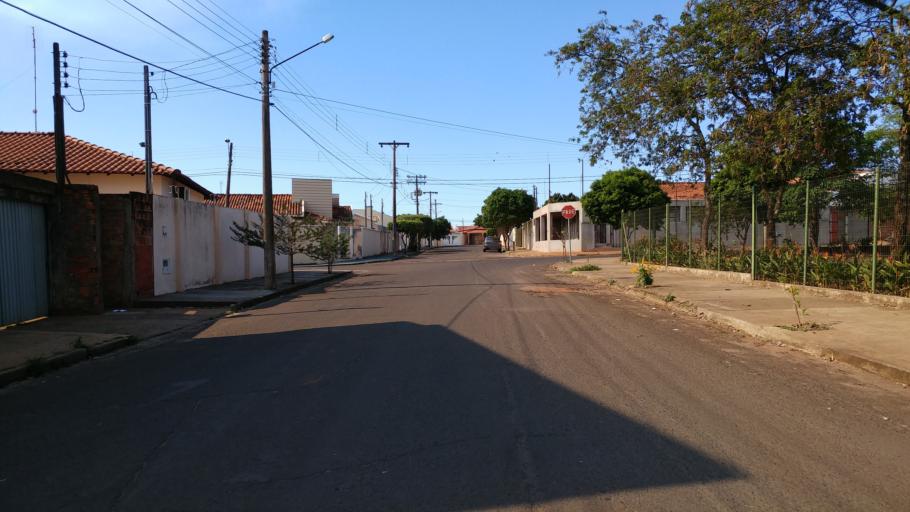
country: BR
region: Sao Paulo
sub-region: Paraguacu Paulista
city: Paraguacu Paulista
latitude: -22.4146
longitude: -50.5876
